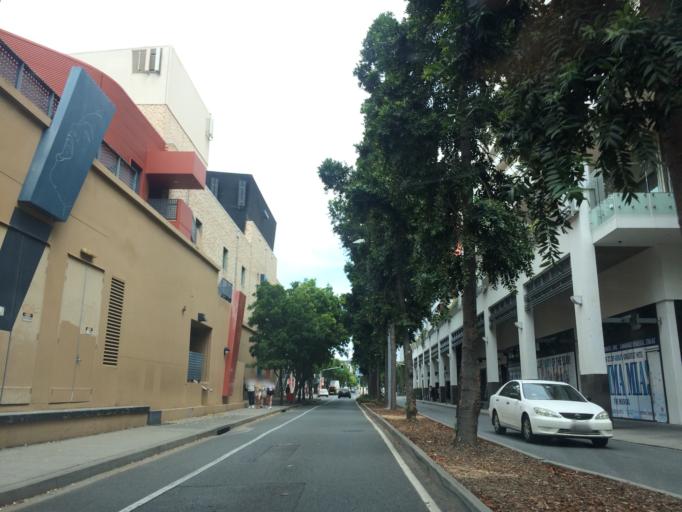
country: AU
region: Queensland
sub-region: Brisbane
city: South Brisbane
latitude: -27.4766
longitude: 153.0202
